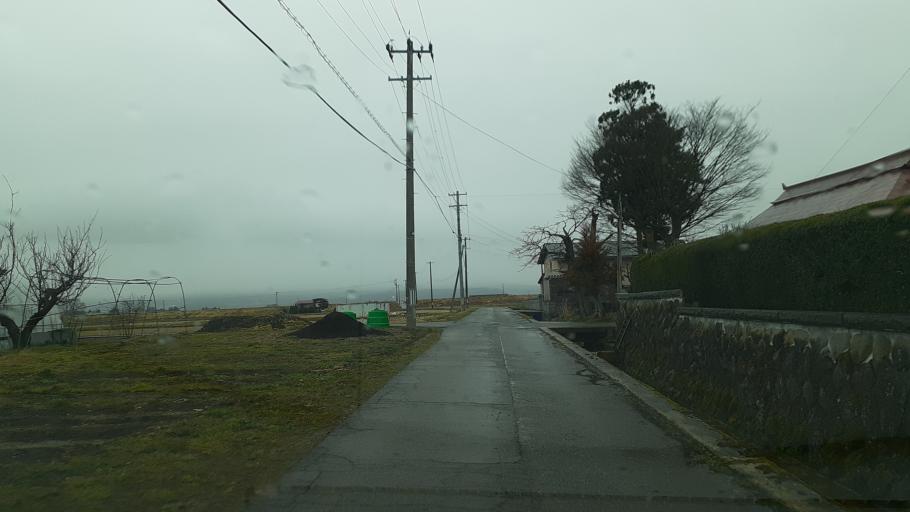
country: JP
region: Fukushima
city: Kitakata
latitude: 37.5841
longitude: 139.8563
